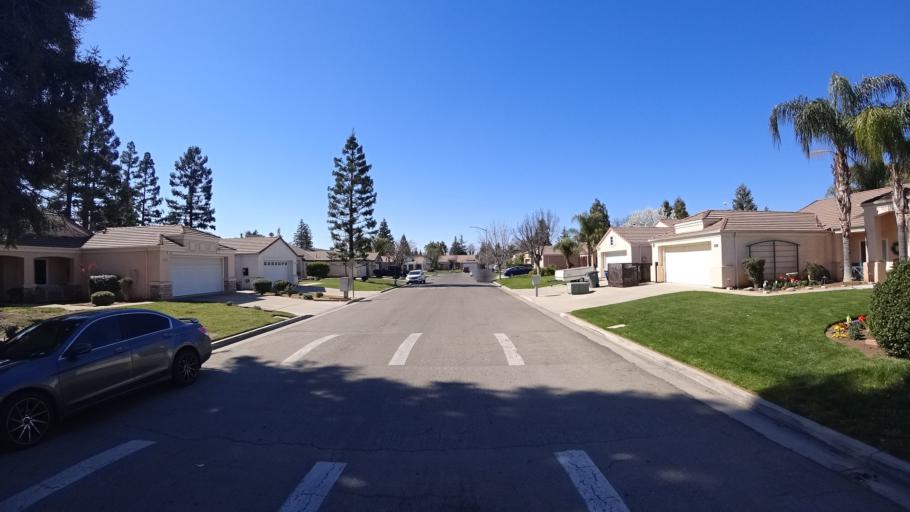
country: US
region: California
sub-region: Fresno County
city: Clovis
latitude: 36.8481
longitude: -119.7416
